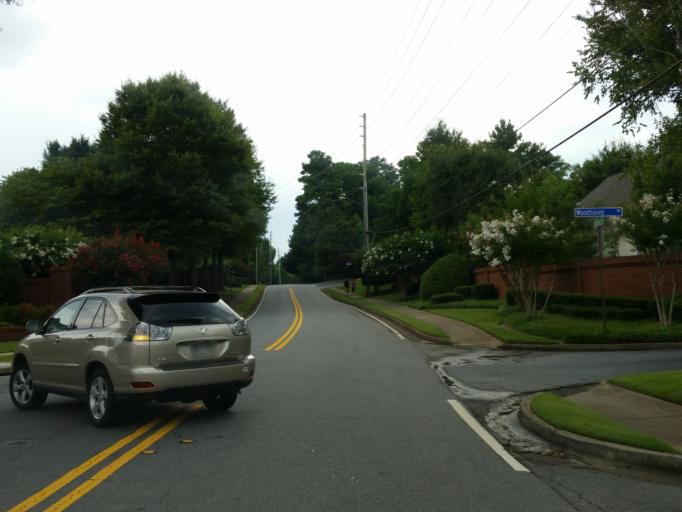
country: US
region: Georgia
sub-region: Fulton County
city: Sandy Springs
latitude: 33.9588
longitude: -84.4171
